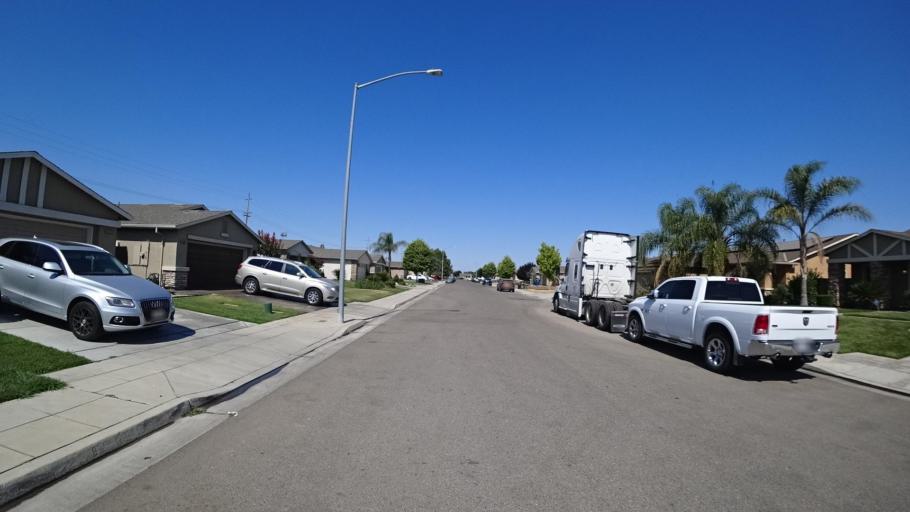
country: US
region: California
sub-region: Fresno County
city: Sunnyside
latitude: 36.7083
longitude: -119.7147
